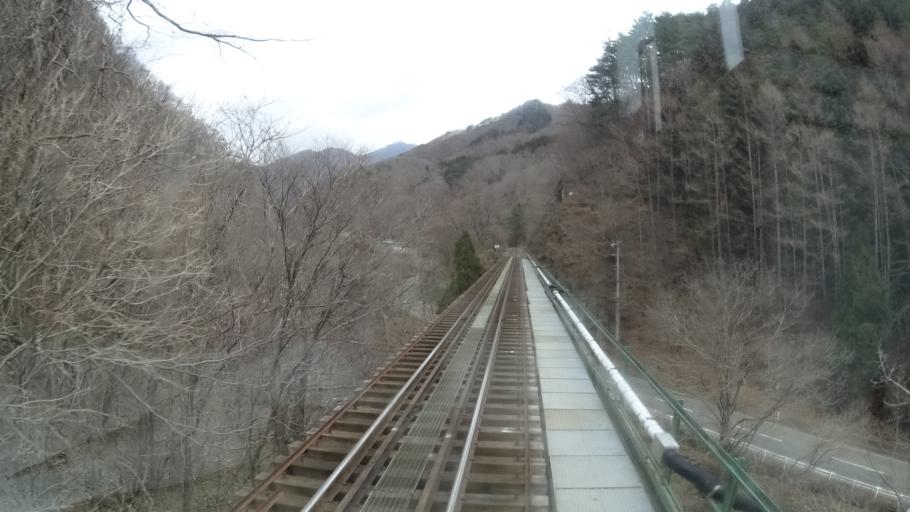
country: JP
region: Iwate
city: Kamaishi
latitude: 39.2716
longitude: 141.7253
